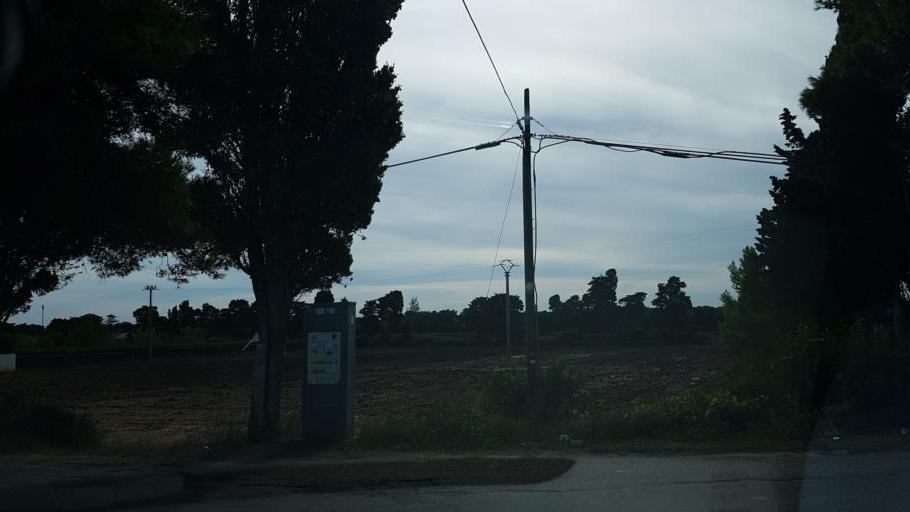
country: IT
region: Apulia
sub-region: Provincia di Lecce
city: Borgagne
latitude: 40.2279
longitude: 18.4427
